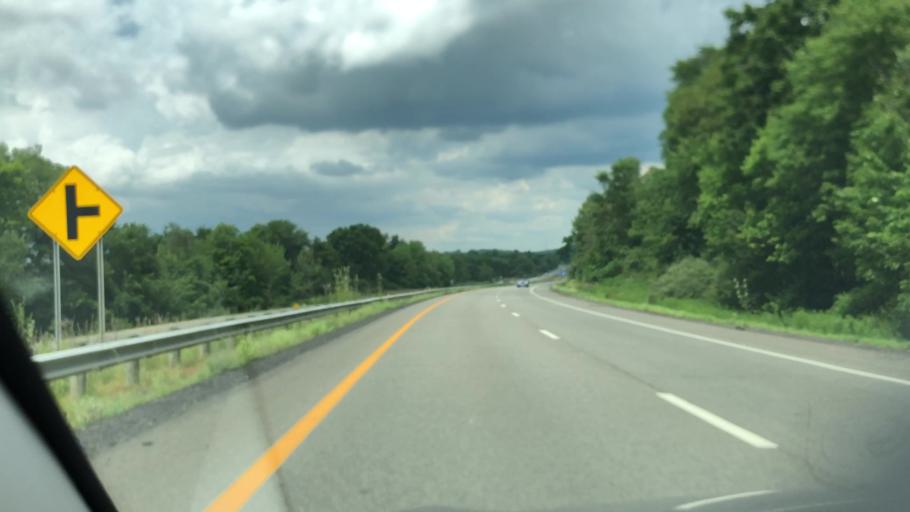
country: US
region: Ohio
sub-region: Summit County
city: Norton
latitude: 41.0768
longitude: -81.6658
